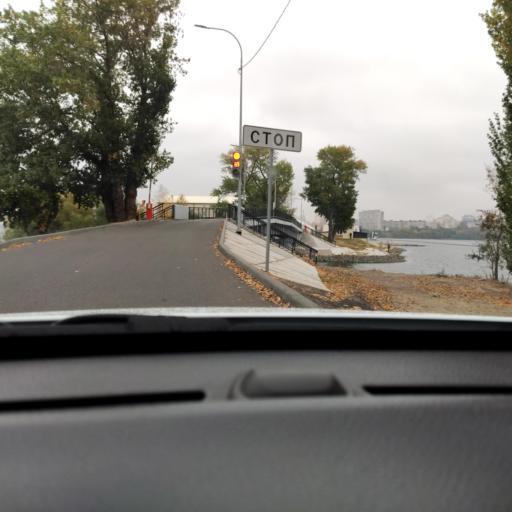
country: RU
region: Voronezj
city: Voronezh
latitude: 51.6692
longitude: 39.2285
